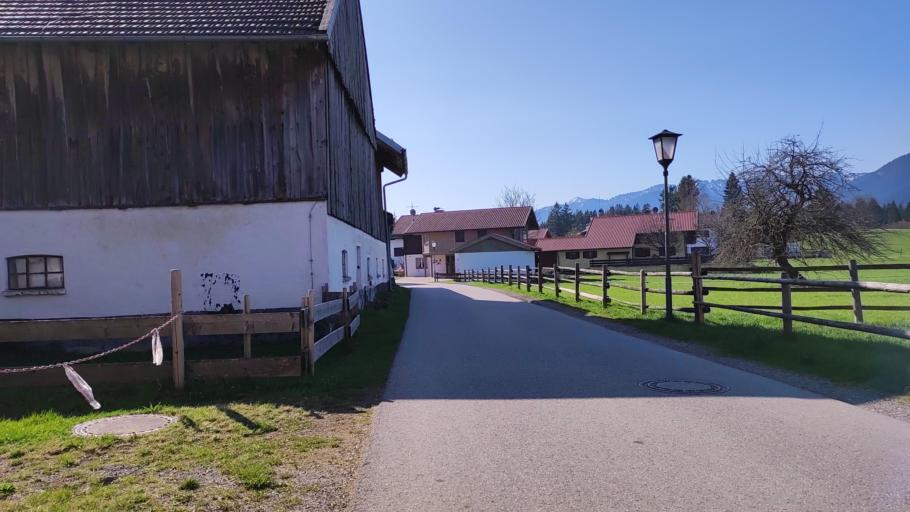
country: DE
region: Bavaria
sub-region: Upper Bavaria
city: Saulgrub
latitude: 47.6483
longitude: 11.0148
